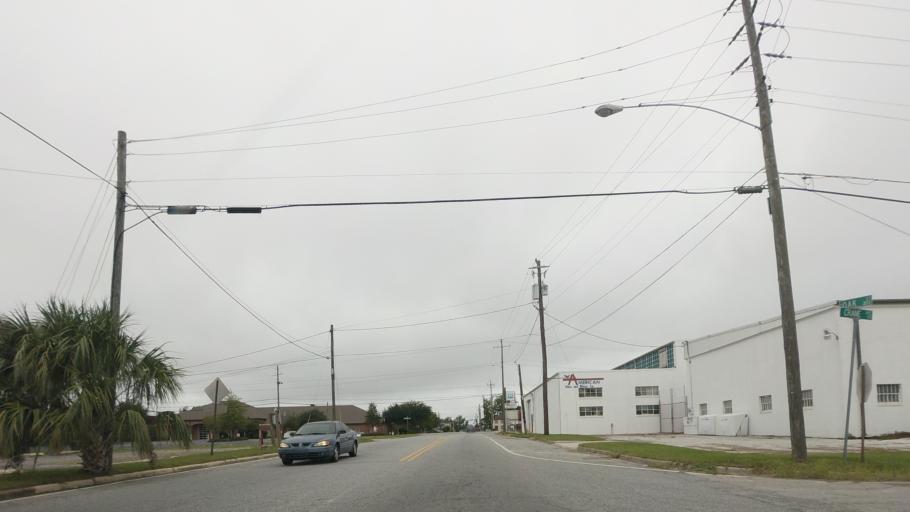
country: US
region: Georgia
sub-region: Lowndes County
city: Valdosta
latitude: 30.8280
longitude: -83.2808
